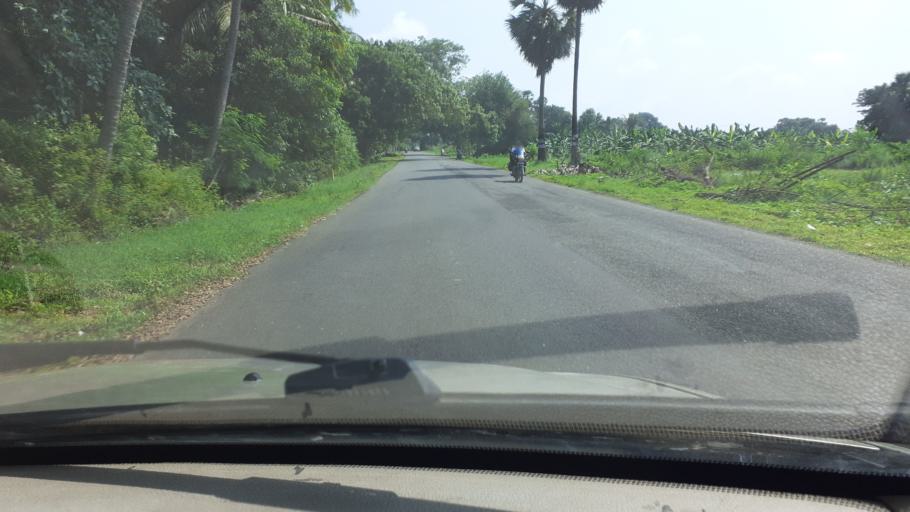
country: IN
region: Tamil Nadu
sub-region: Thoothukkudi
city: Srivaikuntam
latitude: 8.6325
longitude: 77.8840
